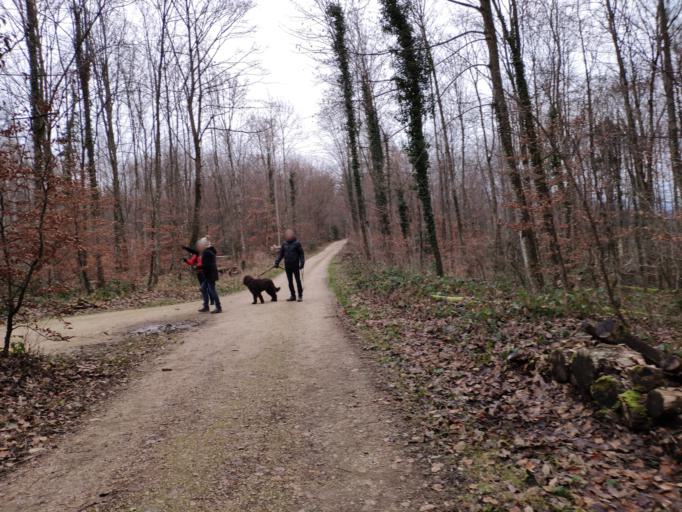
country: CH
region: Basel-City
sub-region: Basel-Stadt
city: Bettingen
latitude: 47.5745
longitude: 7.6772
